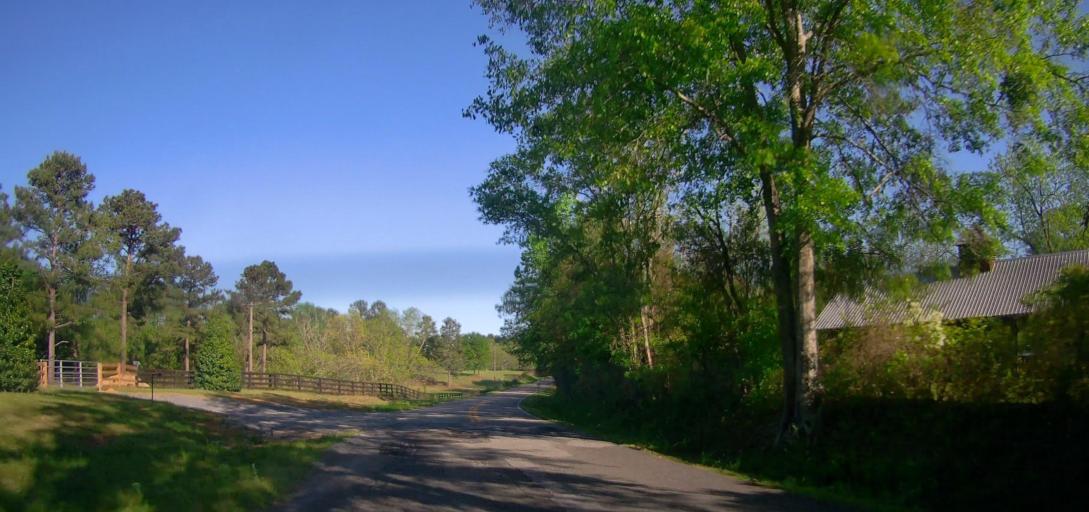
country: US
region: Georgia
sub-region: Houston County
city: Perry
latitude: 32.4805
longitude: -83.7978
